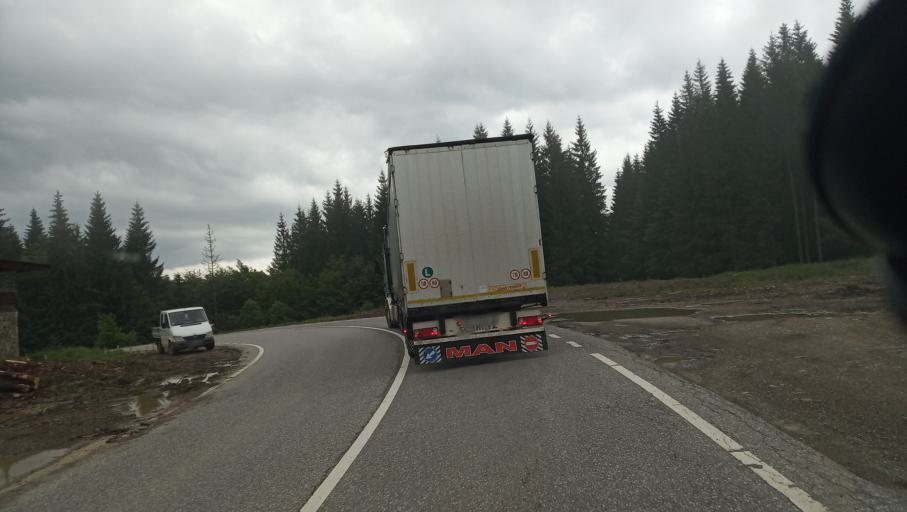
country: RO
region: Neamt
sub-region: Comuna Pipirig
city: Dolhesti
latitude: 47.1697
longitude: 26.0136
